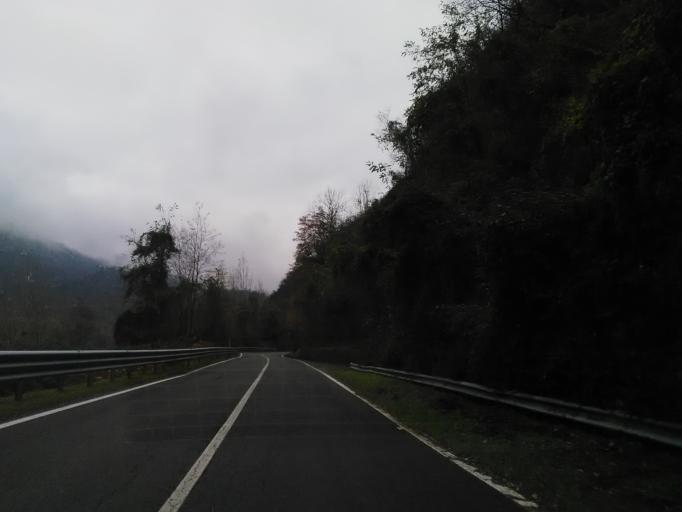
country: IT
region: Piedmont
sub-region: Provincia di Vercelli
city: Varallo
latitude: 45.7987
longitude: 8.2639
